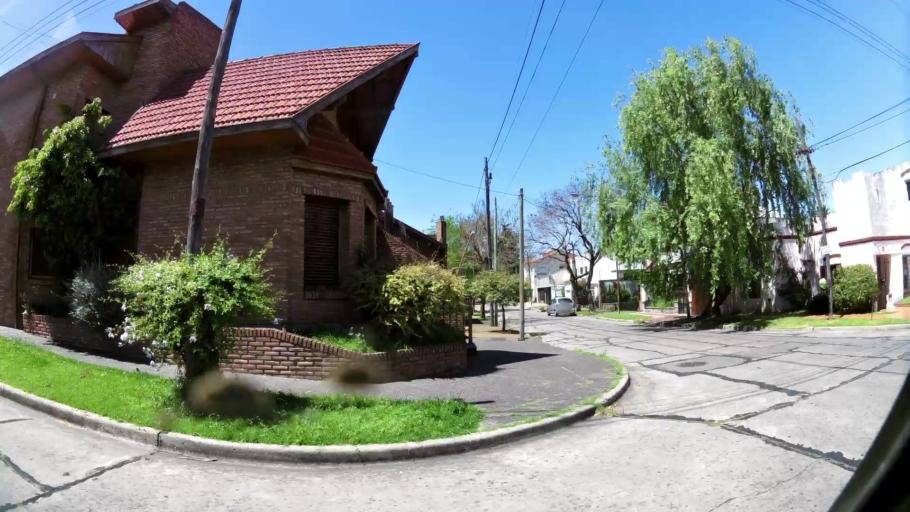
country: AR
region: Buenos Aires
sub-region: Partido de Quilmes
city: Quilmes
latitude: -34.7179
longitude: -58.2844
